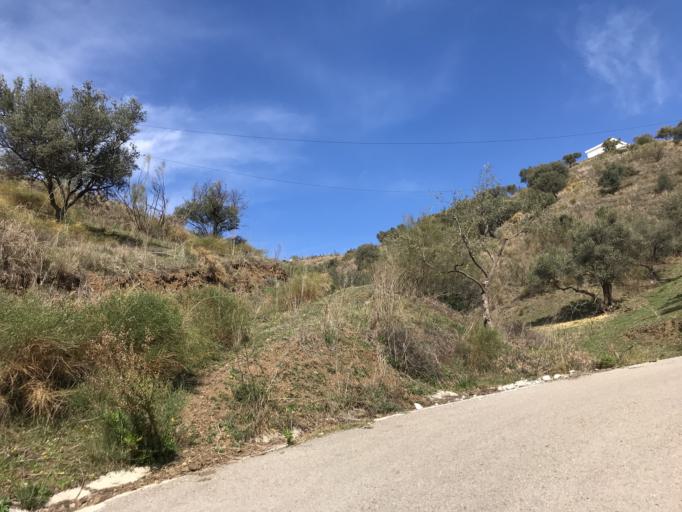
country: ES
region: Andalusia
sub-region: Provincia de Malaga
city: Valdes
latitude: 36.7722
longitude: -4.2162
